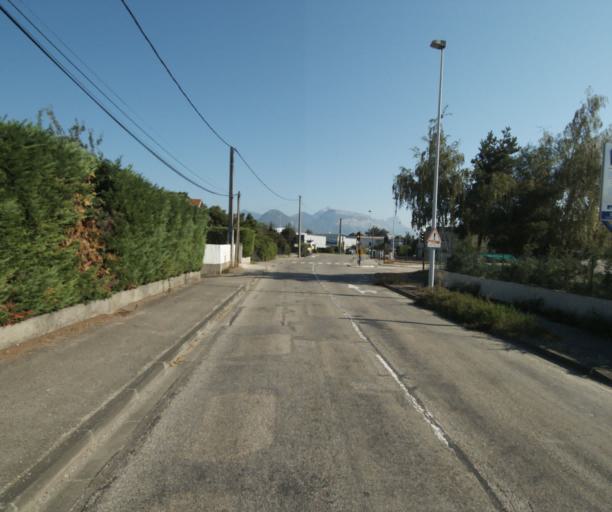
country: FR
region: Rhone-Alpes
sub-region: Departement de l'Isere
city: Le Pont-de-Claix
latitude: 45.1422
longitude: 5.7085
